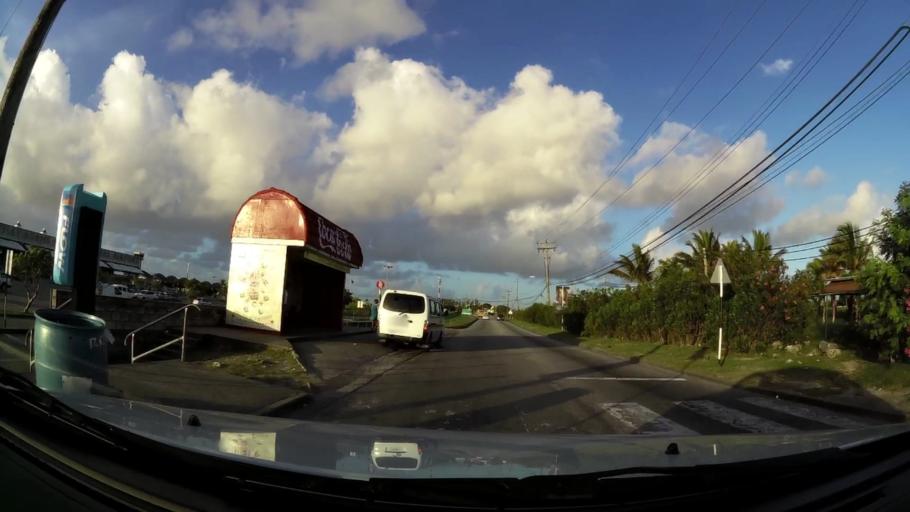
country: BB
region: Saint Philip
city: Crane
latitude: 13.0811
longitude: -59.4886
